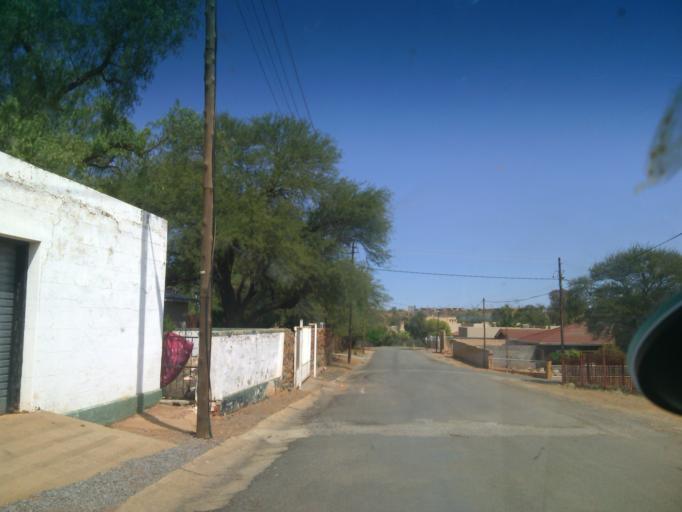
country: ZA
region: Northern Cape
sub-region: Frances Baard District Municipality
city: Barkly West
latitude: -28.5397
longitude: 24.5175
